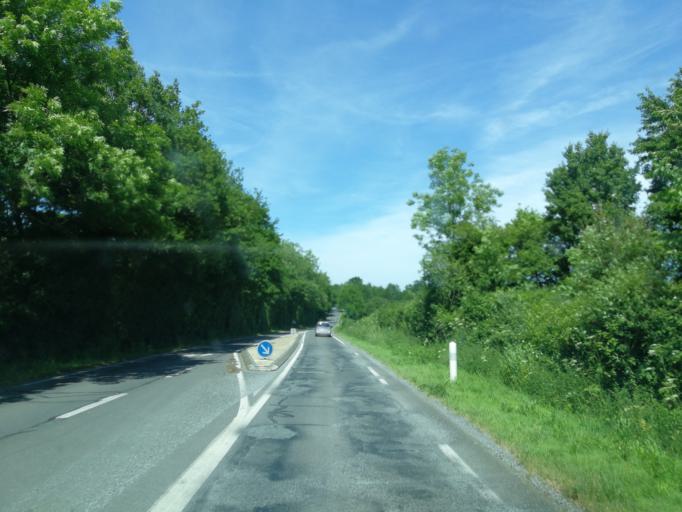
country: FR
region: Pays de la Loire
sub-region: Departement de la Vendee
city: Saint-Pierre-du-Chemin
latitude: 46.7219
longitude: -0.6768
